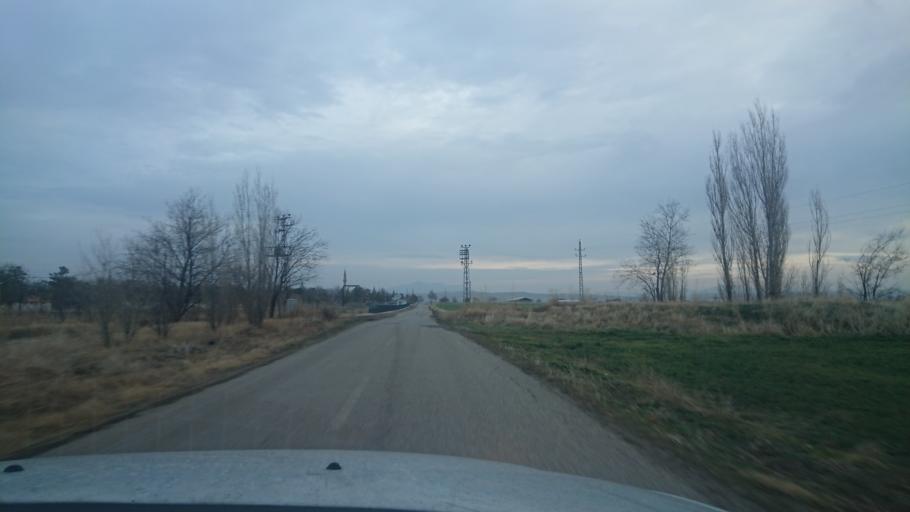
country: TR
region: Aksaray
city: Yesilova
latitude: 38.4543
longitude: 33.8377
